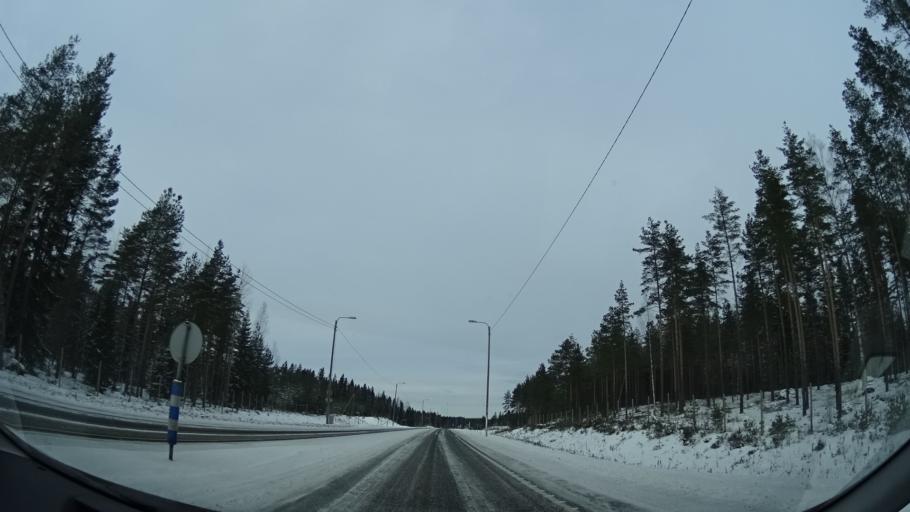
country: FI
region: Uusimaa
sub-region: Helsinki
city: Kaerkoelae
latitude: 60.6359
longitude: 23.9020
